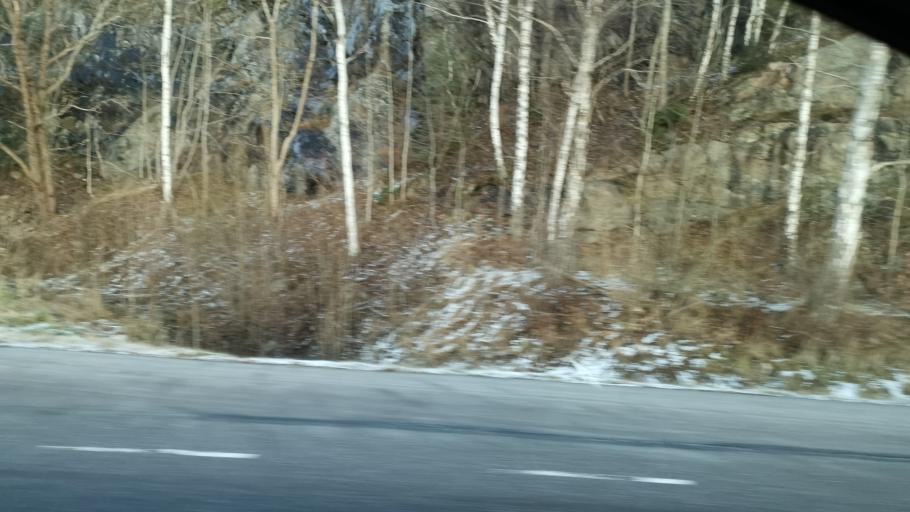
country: SE
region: Vaestra Goetaland
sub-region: Munkedals Kommun
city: Munkedal
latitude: 58.4398
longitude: 11.7056
